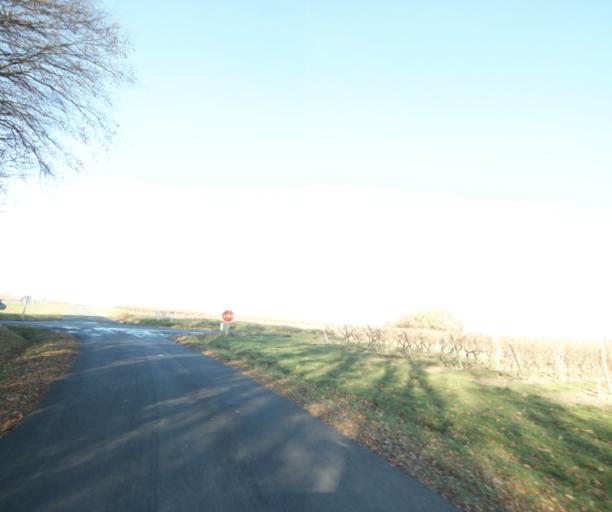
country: FR
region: Poitou-Charentes
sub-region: Departement de la Charente-Maritime
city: Cherac
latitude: 45.7325
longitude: -0.4516
